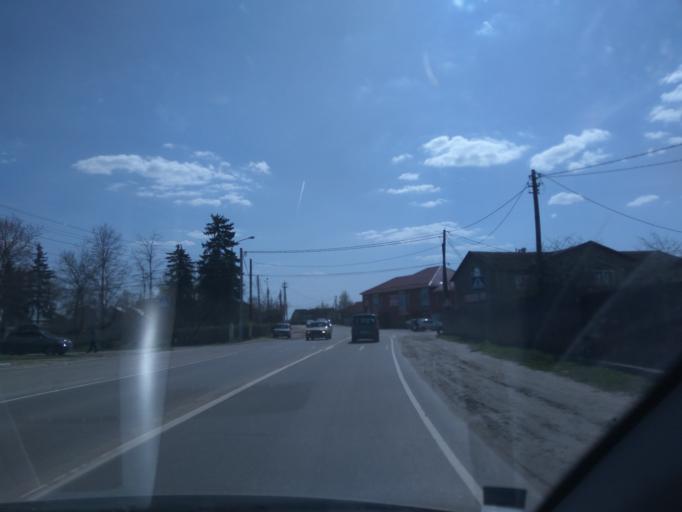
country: RU
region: Moskovskaya
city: Ramenskoye
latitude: 55.5457
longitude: 38.2344
